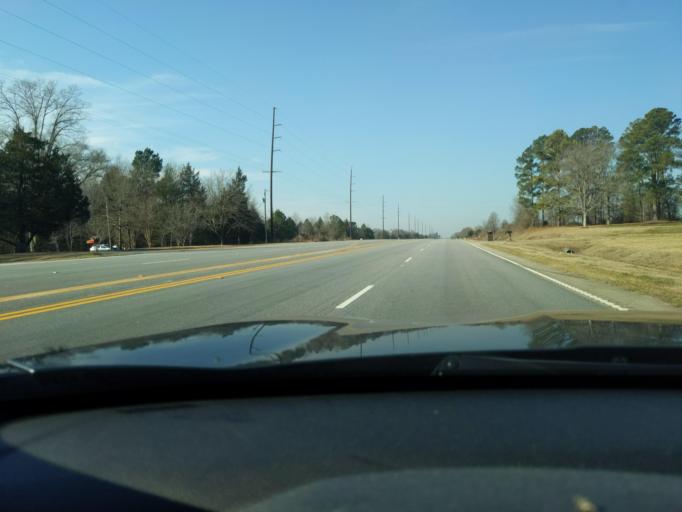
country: US
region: South Carolina
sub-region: Abbeville County
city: Calhoun Falls
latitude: 34.1043
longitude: -82.5360
